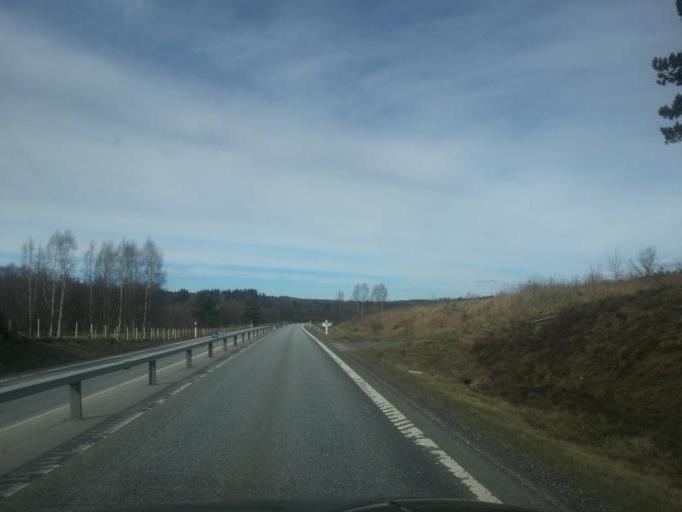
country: SE
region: Joenkoeping
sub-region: Jonkopings Kommun
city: Bankeryd
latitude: 57.8566
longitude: 14.1041
